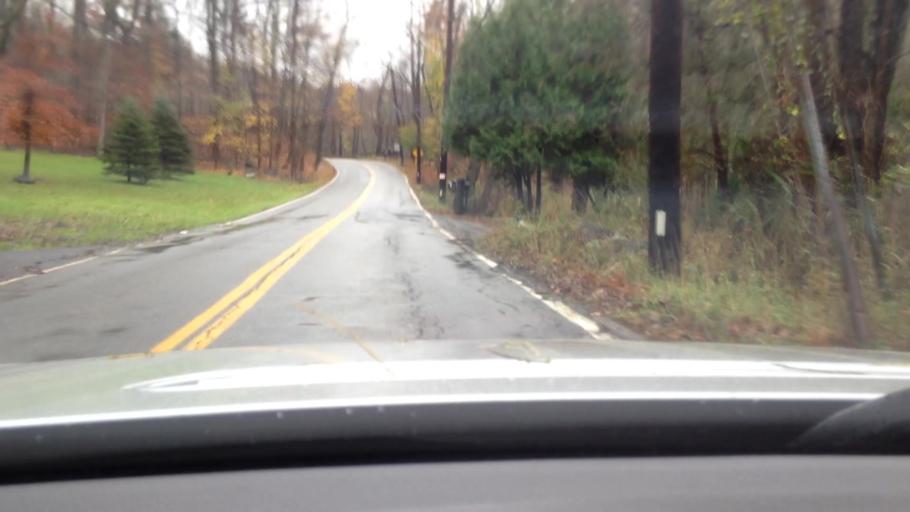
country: US
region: New York
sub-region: Westchester County
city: Croton-on-Hudson
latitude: 41.2352
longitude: -73.8927
